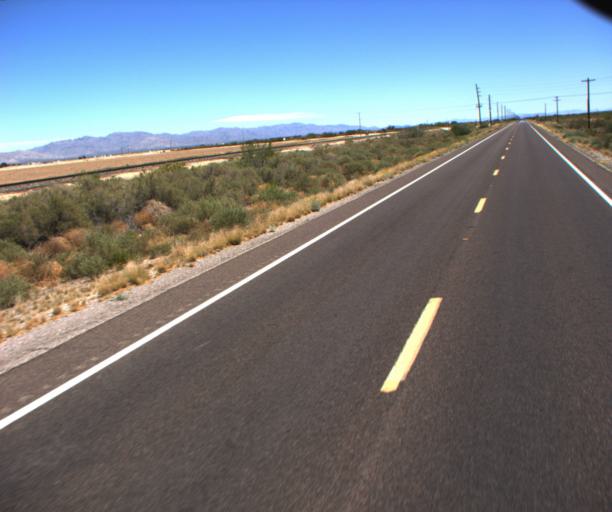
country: US
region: Arizona
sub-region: La Paz County
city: Salome
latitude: 33.7925
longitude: -113.5952
